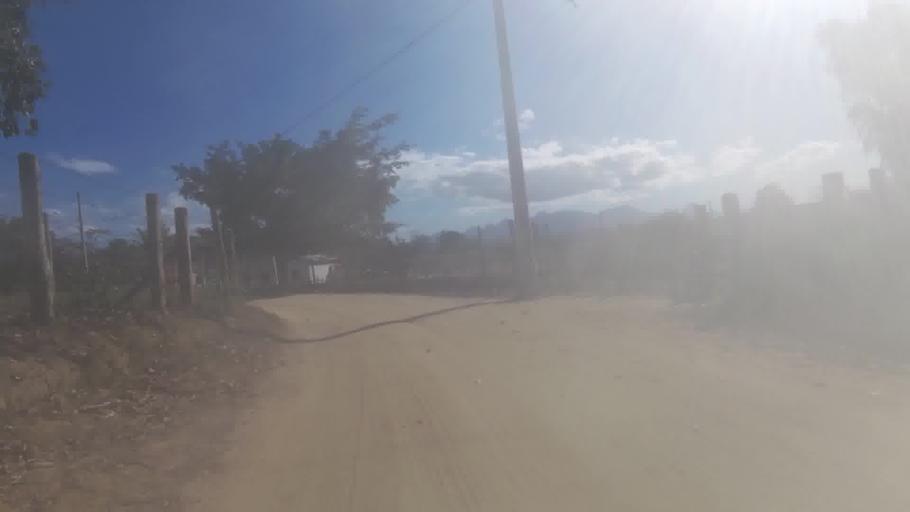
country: BR
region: Espirito Santo
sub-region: Cachoeiro De Itapemirim
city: Cachoeiro de Itapemirim
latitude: -21.0179
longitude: -41.0385
